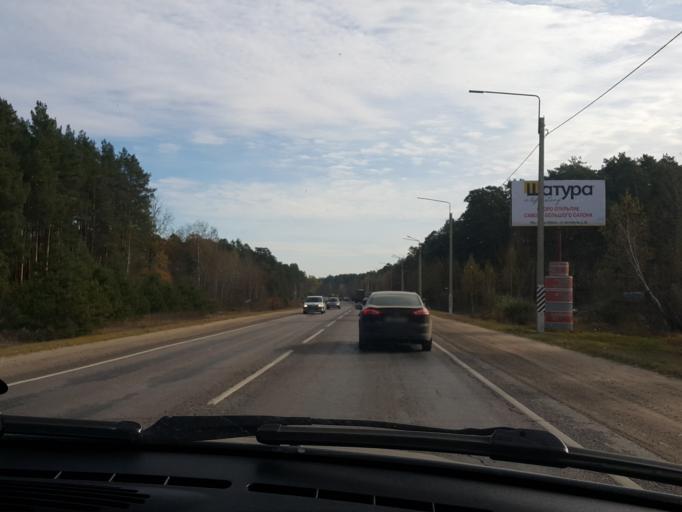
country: RU
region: Tambov
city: Donskoye
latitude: 52.7104
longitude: 41.5279
